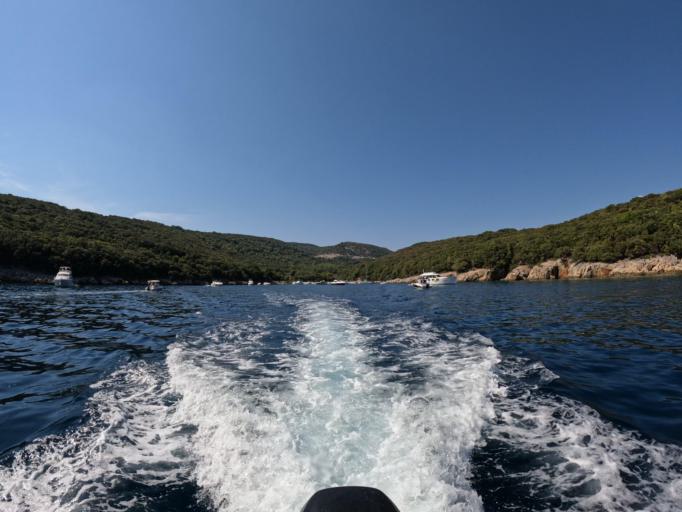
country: HR
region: Primorsko-Goranska
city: Cres
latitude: 44.9498
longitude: 14.4640
